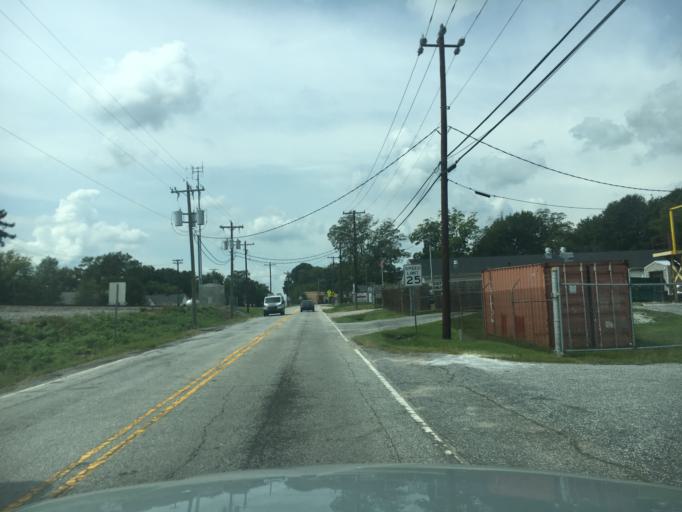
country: US
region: South Carolina
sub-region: Greenville County
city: Greer
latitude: 34.9353
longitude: -82.2175
